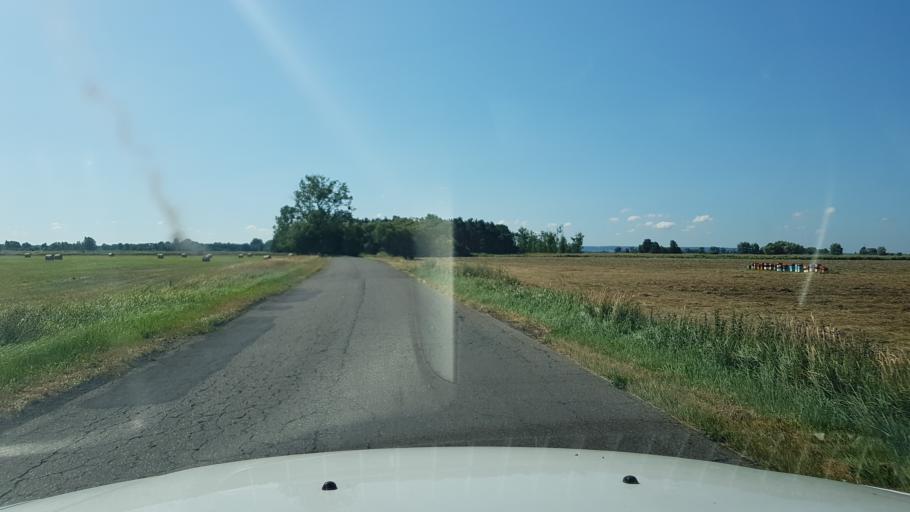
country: PL
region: West Pomeranian Voivodeship
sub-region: Powiat goleniowski
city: Goleniow
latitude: 53.4873
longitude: 14.7115
